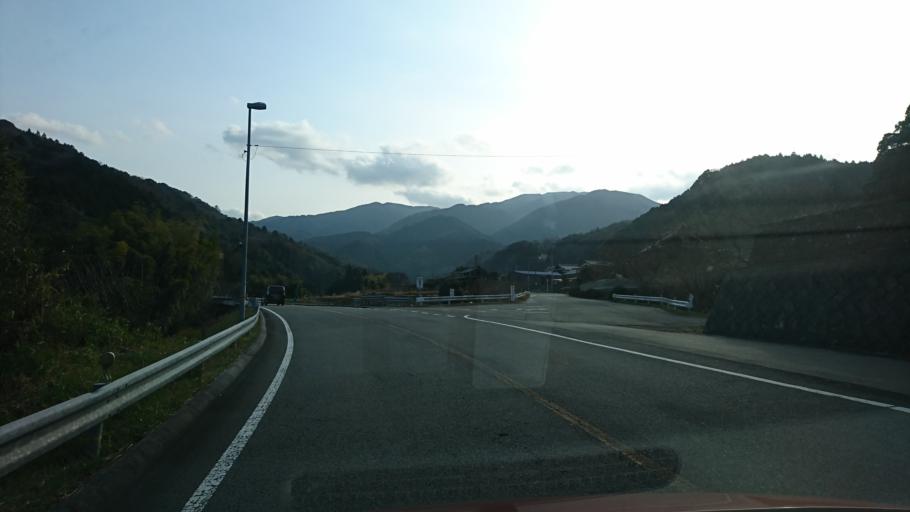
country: JP
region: Ehime
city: Hojo
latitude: 33.9797
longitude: 132.9048
